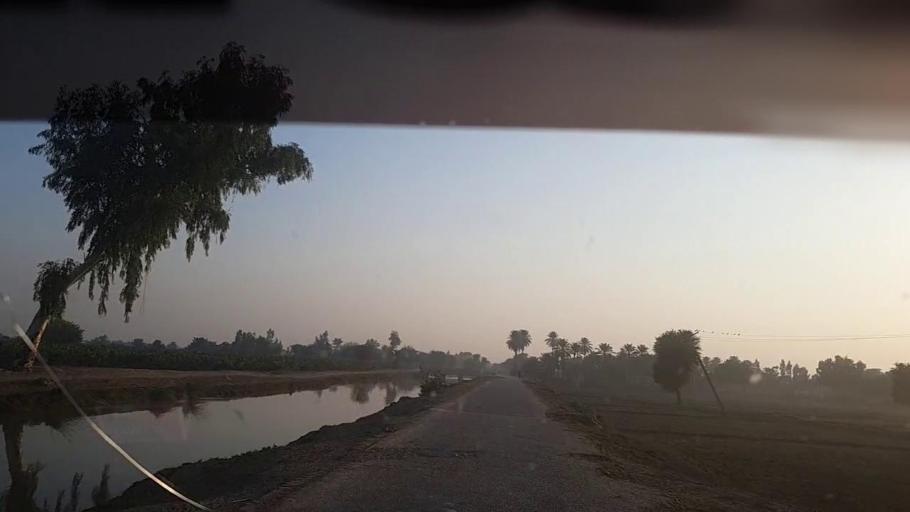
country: PK
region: Sindh
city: Ranipur
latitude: 27.2350
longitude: 68.5490
